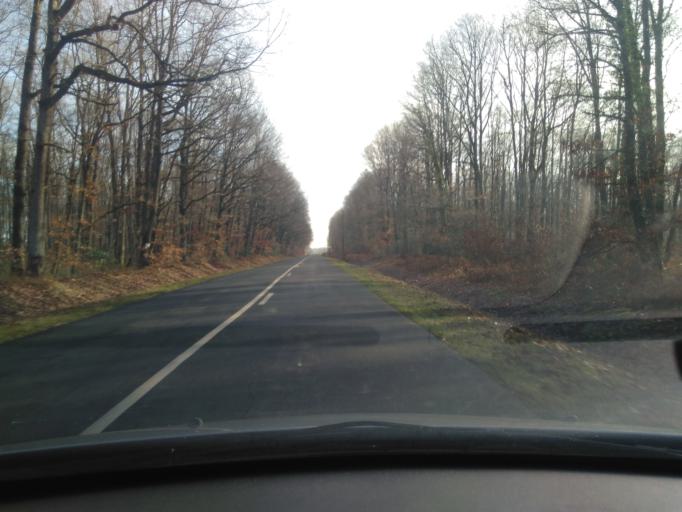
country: FR
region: Centre
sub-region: Departement du Cher
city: Chateaumeillant
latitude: 46.6382
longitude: 2.1053
